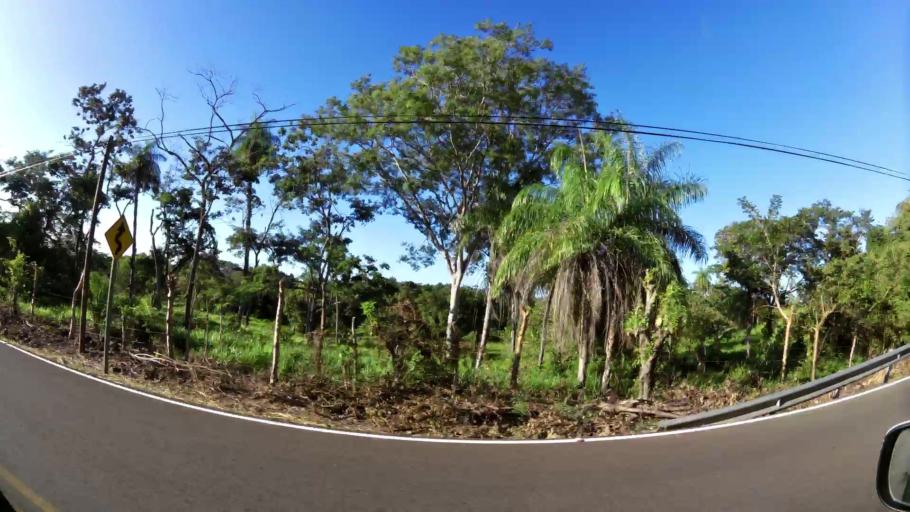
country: CR
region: Puntarenas
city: Miramar
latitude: 10.1462
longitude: -84.8510
